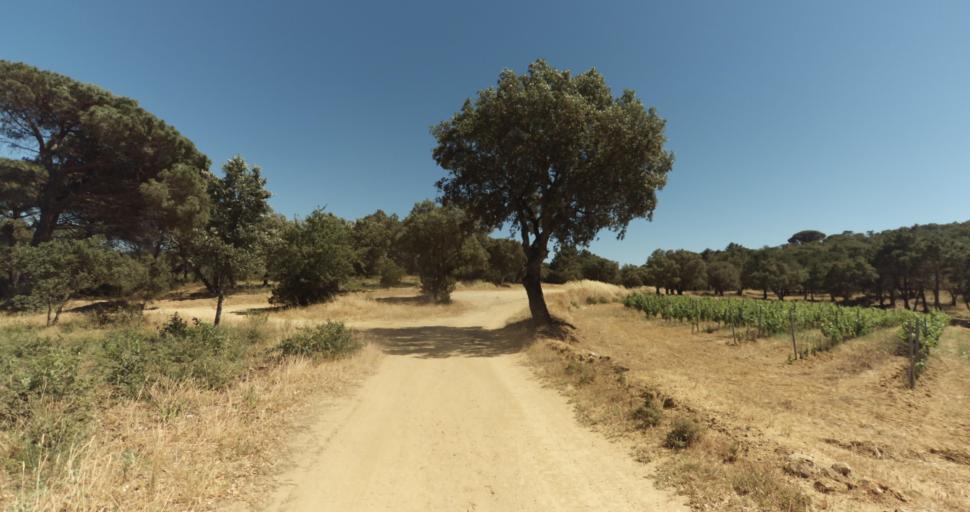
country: FR
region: Provence-Alpes-Cote d'Azur
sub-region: Departement du Var
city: Gassin
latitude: 43.2444
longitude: 6.5606
